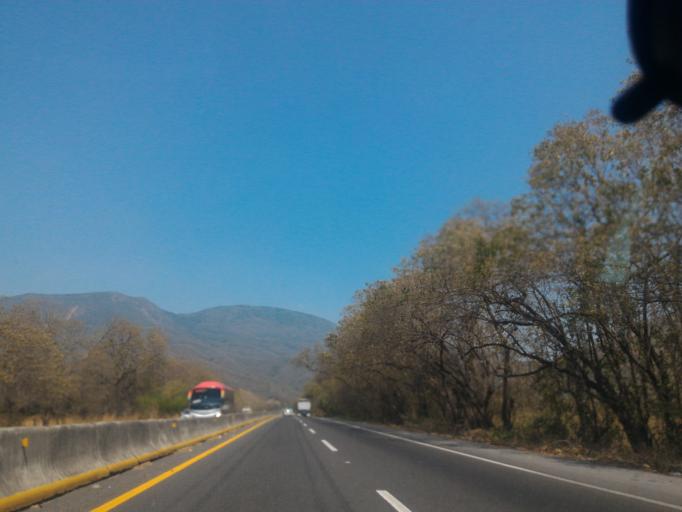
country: MX
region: Colima
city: Madrid
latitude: 19.0079
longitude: -103.8335
